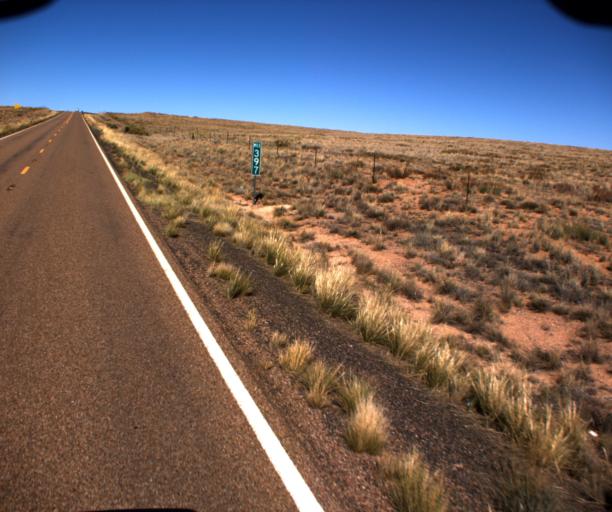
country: US
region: Arizona
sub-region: Navajo County
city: Holbrook
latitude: 34.9992
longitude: -110.0894
